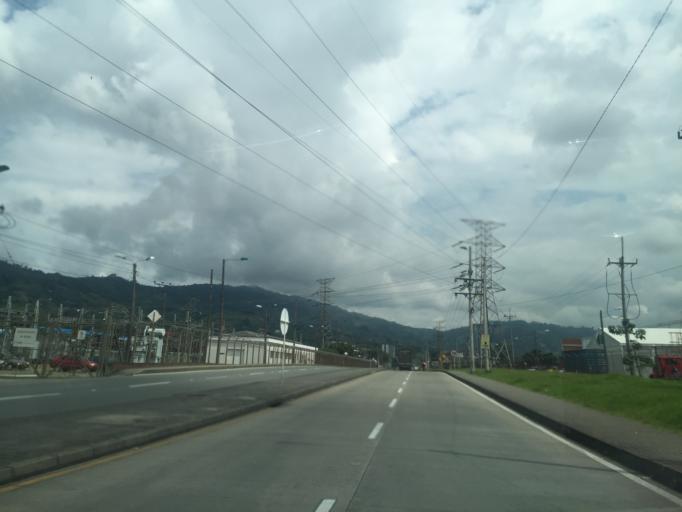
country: CO
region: Risaralda
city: Dos Quebradas
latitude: 4.8341
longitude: -75.6787
